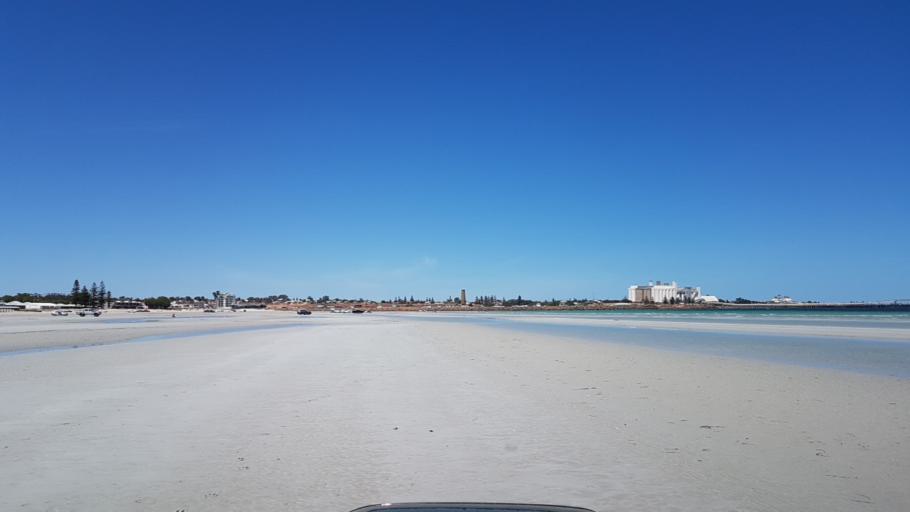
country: AU
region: South Australia
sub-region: Copper Coast
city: Wallaroo
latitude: -33.9141
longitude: 137.6295
